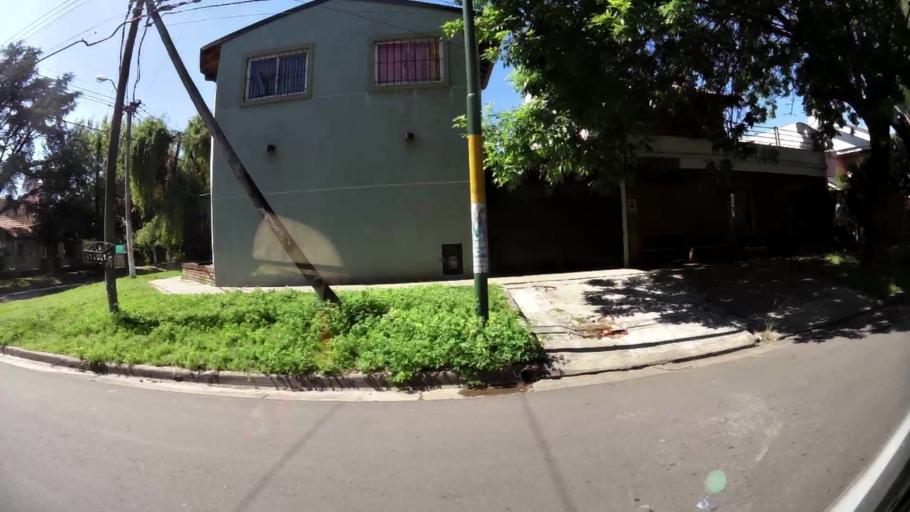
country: AR
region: Buenos Aires
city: Ituzaingo
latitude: -34.6655
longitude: -58.6683
